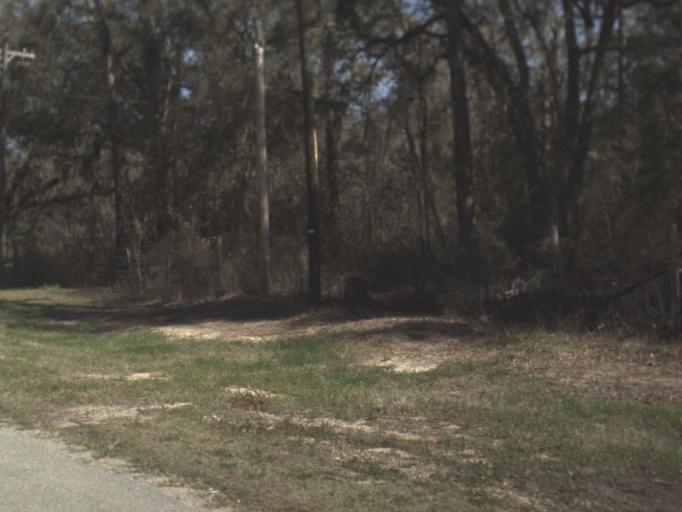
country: US
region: Florida
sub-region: Jefferson County
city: Monticello
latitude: 30.3903
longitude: -84.0118
